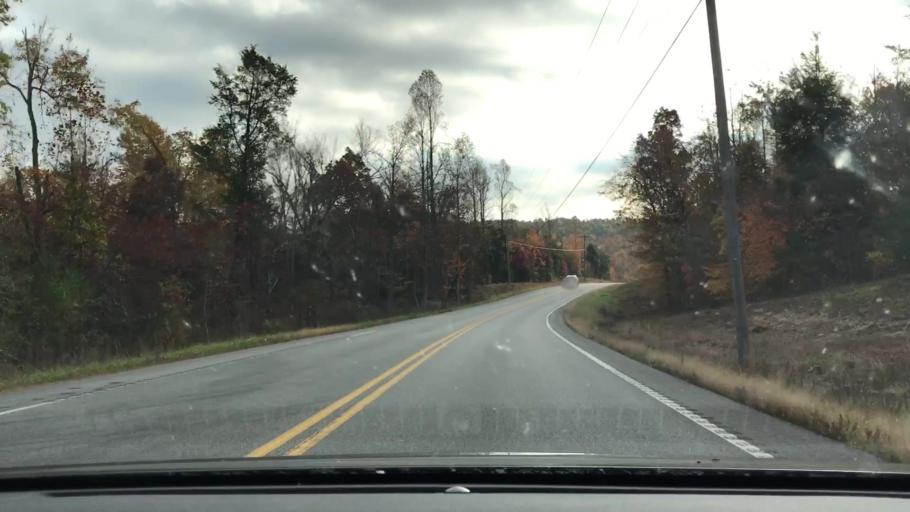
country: US
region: Tennessee
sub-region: Putnam County
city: Monterey
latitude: 36.1324
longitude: -85.2104
